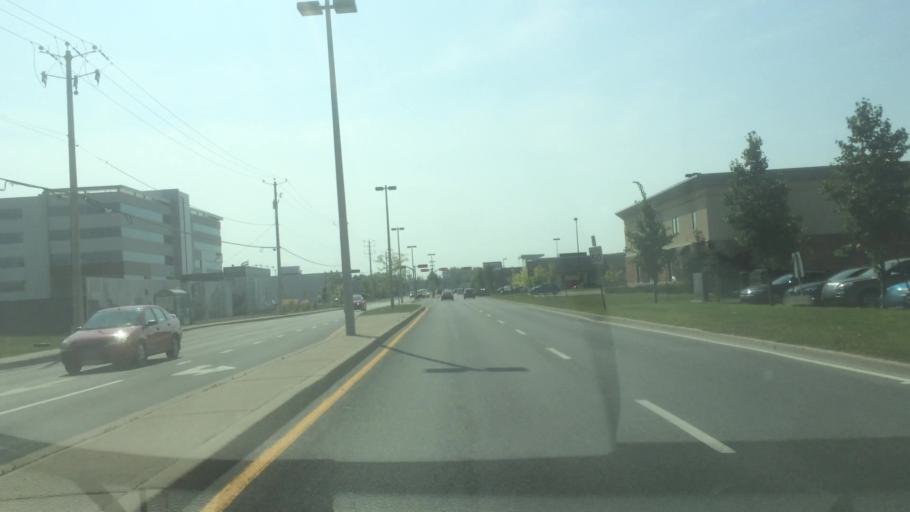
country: CA
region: Quebec
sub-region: Monteregie
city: Vaudreuil-Dorion
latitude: 45.3959
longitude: -74.0546
